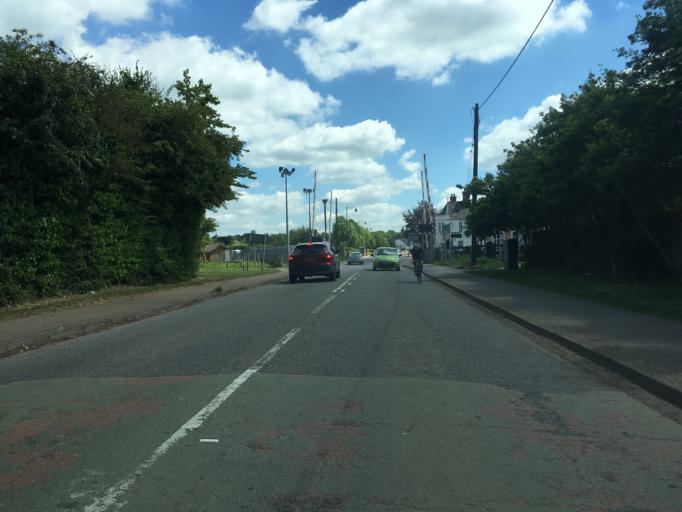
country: GB
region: England
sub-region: Milton Keynes
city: Woburn Sands
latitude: 52.0185
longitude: -0.6545
